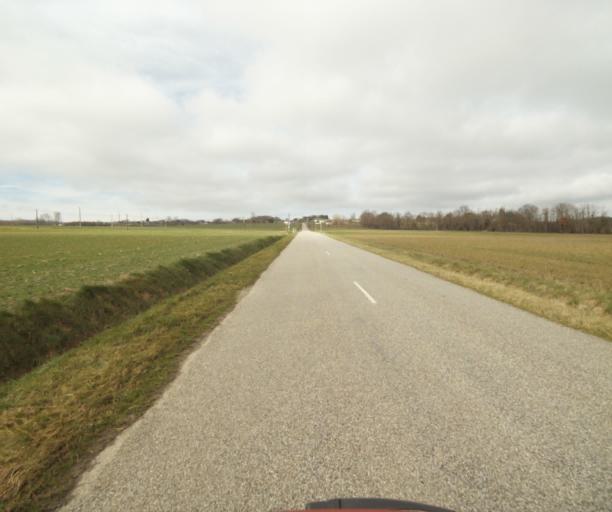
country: FR
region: Midi-Pyrenees
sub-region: Departement de l'Ariege
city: Pamiers
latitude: 43.1083
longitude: 1.5359
